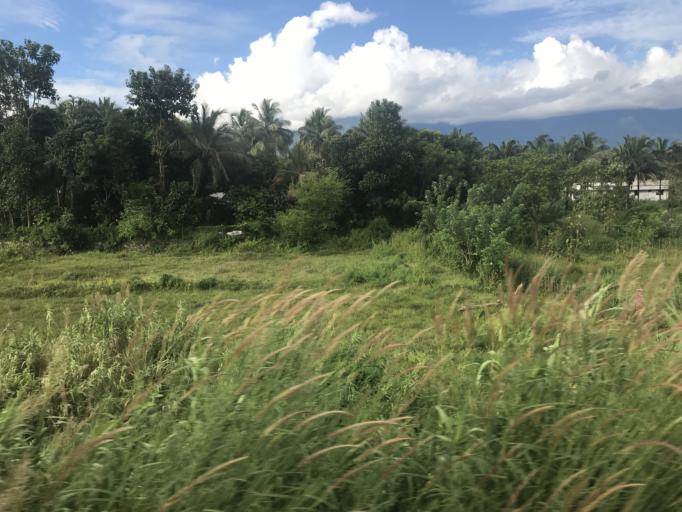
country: IN
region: Kerala
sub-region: Palakkad district
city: Palakkad
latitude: 10.8155
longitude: 76.6783
